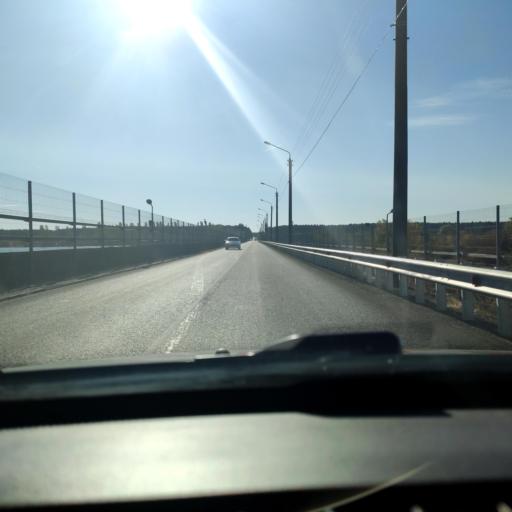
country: RU
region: Voronezj
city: Shilovo
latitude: 51.5428
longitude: 39.1372
